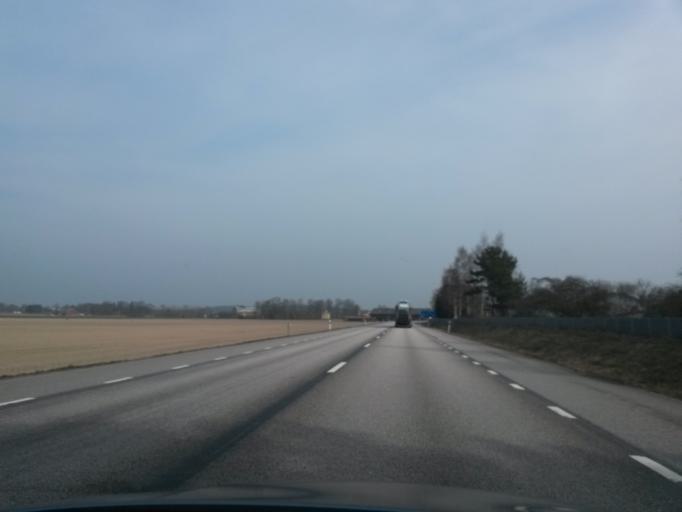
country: SE
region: Vaestra Goetaland
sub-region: Gullspangs Kommun
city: Hova
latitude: 58.8566
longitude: 14.2091
